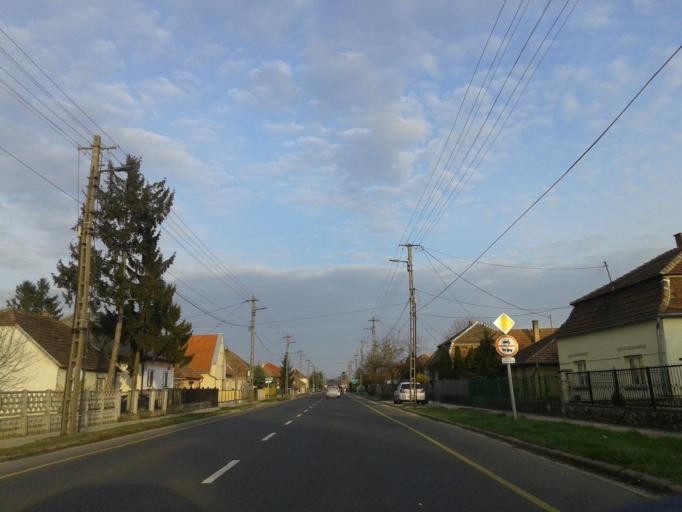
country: HU
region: Komarom-Esztergom
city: Komarom
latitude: 47.7364
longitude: 18.1511
